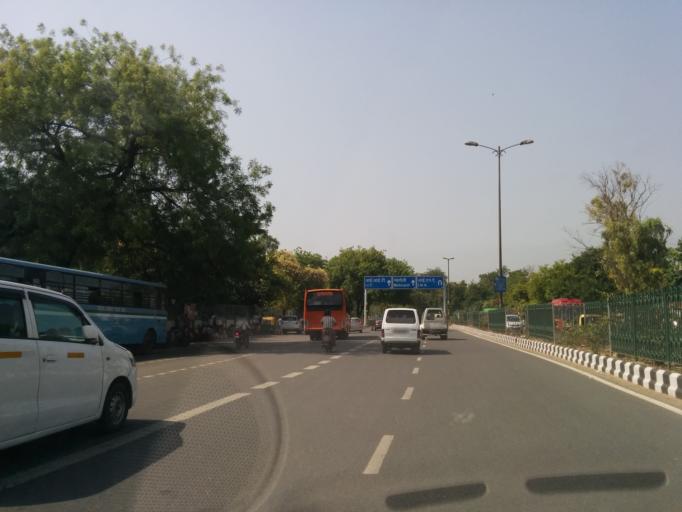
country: IN
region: NCT
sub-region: New Delhi
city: New Delhi
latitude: 28.5666
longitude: 77.2078
